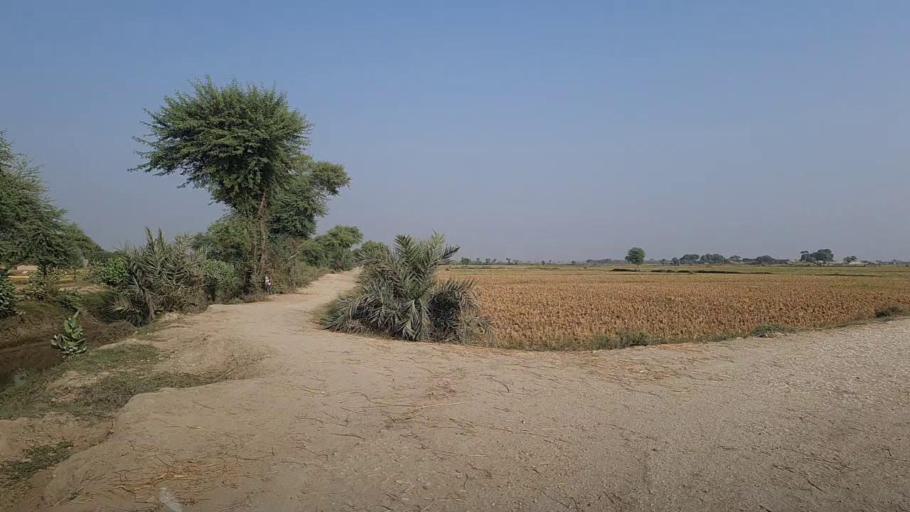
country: PK
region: Sindh
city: Kandhkot
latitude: 28.3029
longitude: 69.2488
